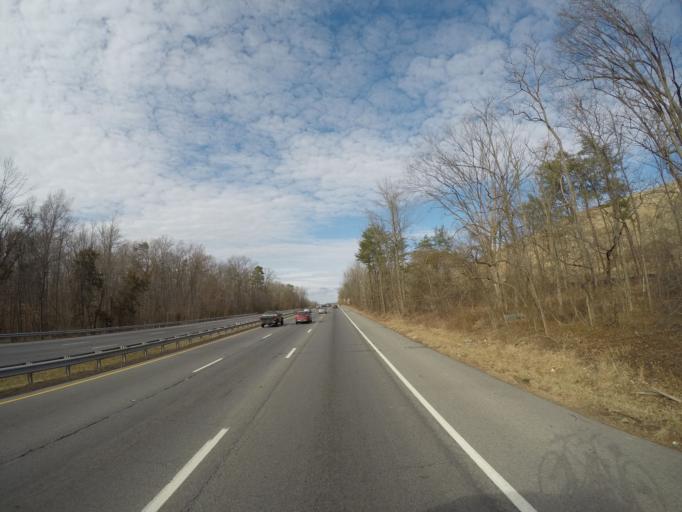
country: US
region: Maryland
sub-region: Prince George's County
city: Friendly
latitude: 38.7513
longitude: -76.9926
